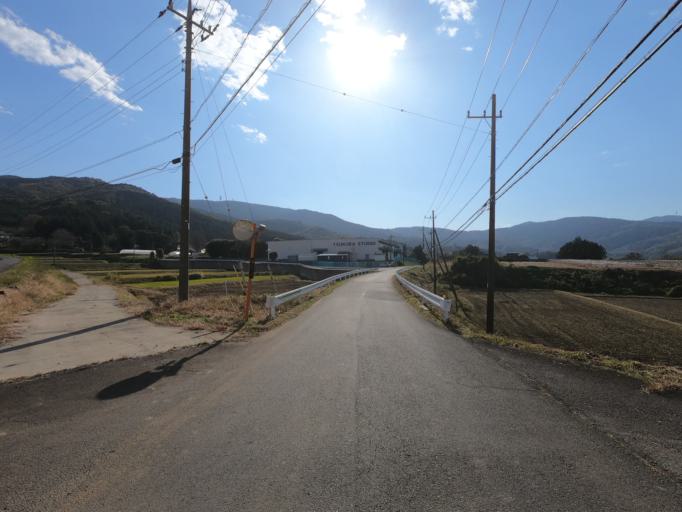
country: JP
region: Ibaraki
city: Tsukuba
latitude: 36.1915
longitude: 140.1818
